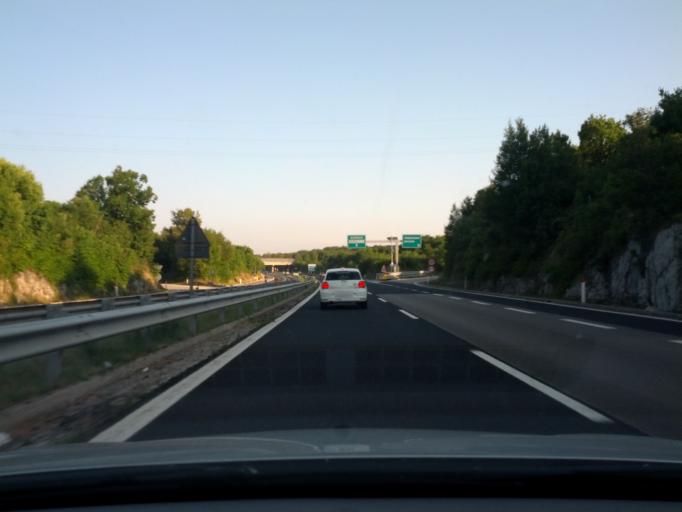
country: IT
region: Friuli Venezia Giulia
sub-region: Provincia di Trieste
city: Villa Opicina
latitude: 45.6756
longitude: 13.8191
